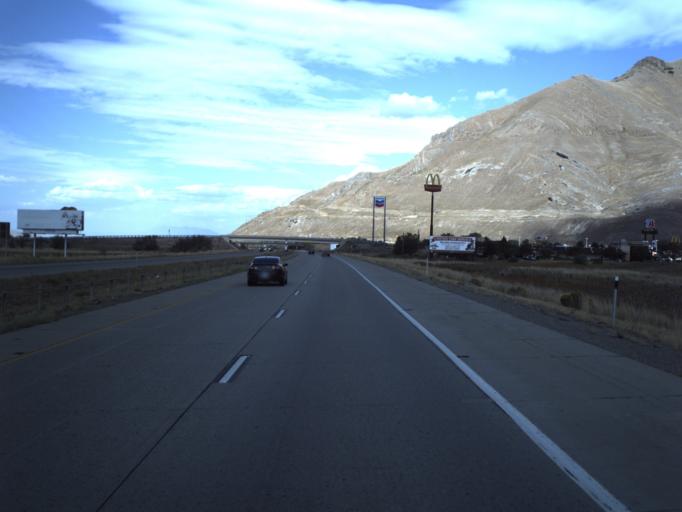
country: US
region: Utah
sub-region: Tooele County
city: Stansbury park
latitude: 40.6862
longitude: -112.2708
